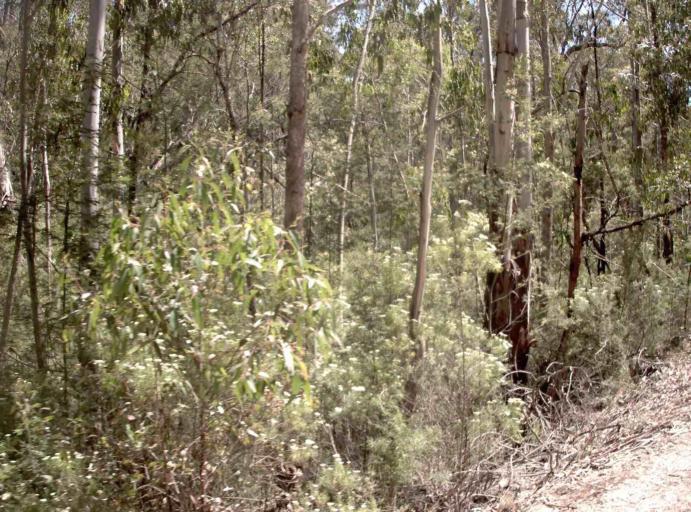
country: AU
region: Victoria
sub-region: East Gippsland
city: Lakes Entrance
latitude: -37.3600
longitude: 148.2227
